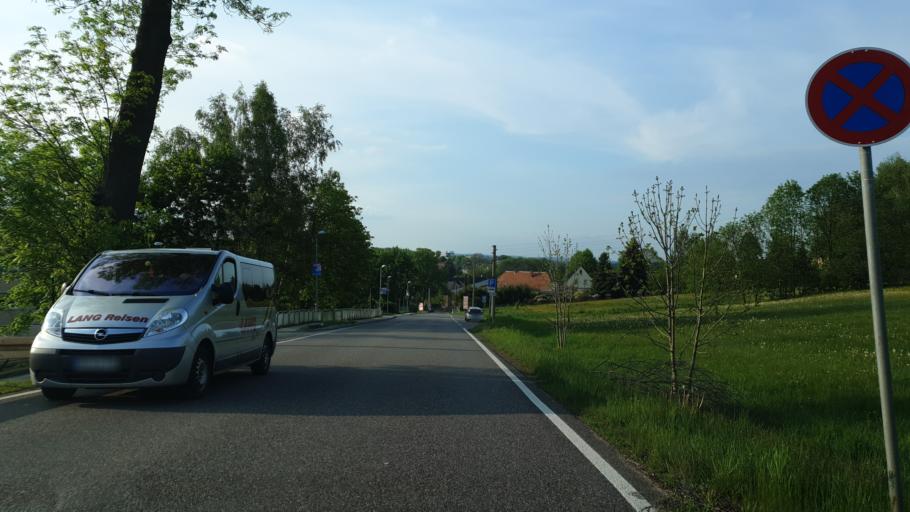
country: DE
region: Saxony
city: Stollberg
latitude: 50.7075
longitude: 12.7844
